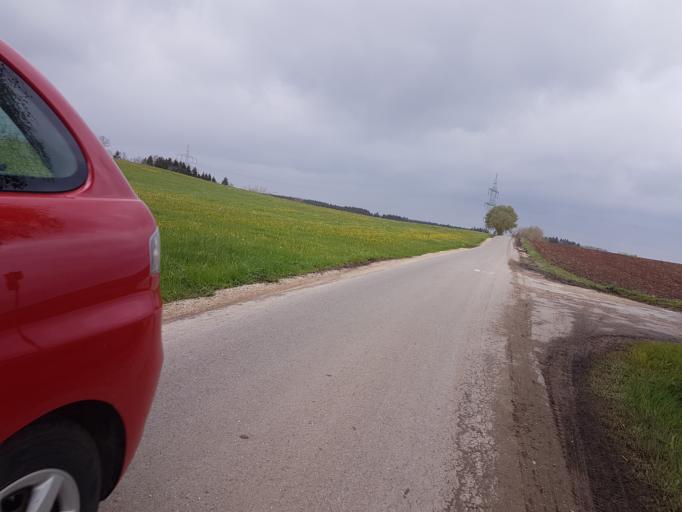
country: DE
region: Baden-Wuerttemberg
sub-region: Freiburg Region
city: Hufingen
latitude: 47.9094
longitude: 8.5206
